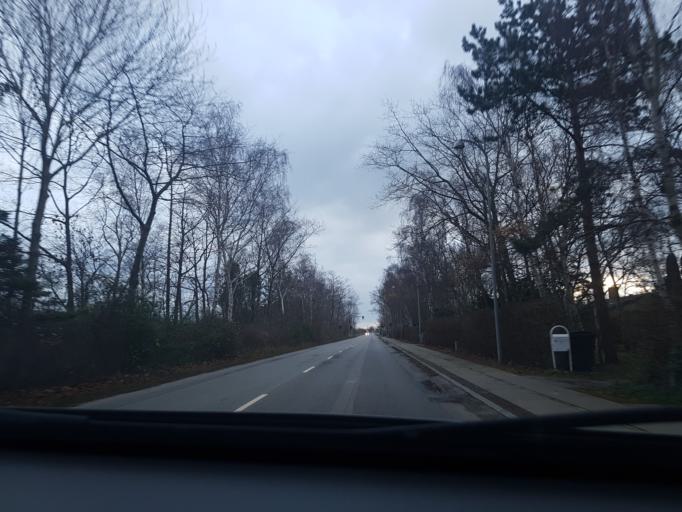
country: DK
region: Capital Region
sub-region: Ishoj Kommune
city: Ishoj
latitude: 55.6108
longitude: 12.3696
